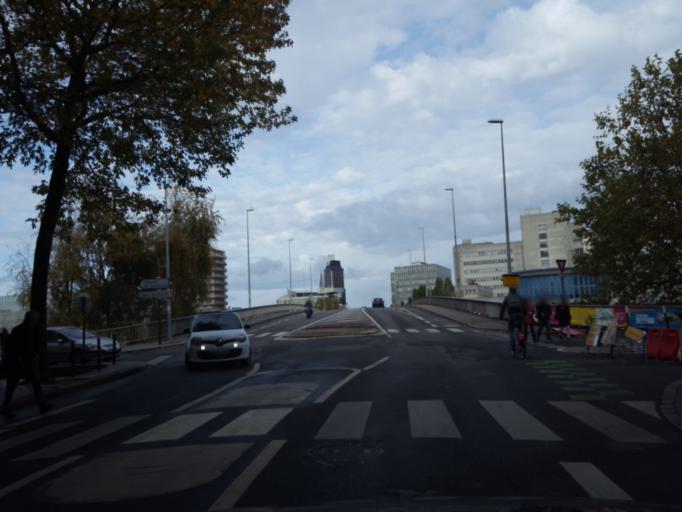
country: FR
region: Pays de la Loire
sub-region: Departement de la Loire-Atlantique
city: Nantes
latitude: 47.2070
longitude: -1.5550
